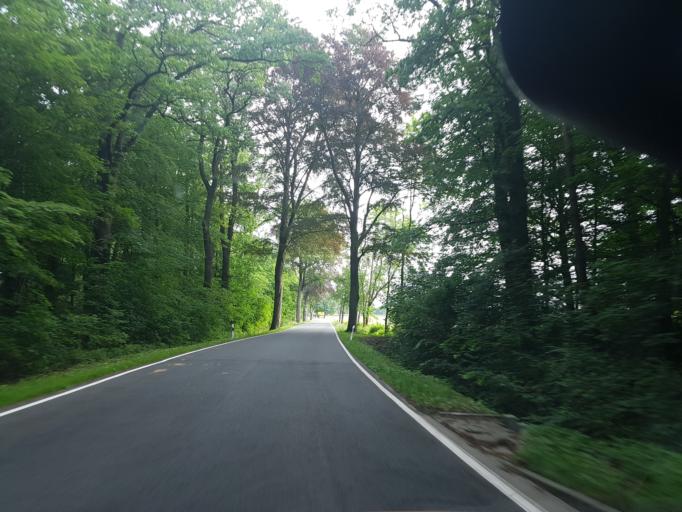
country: DE
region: Brandenburg
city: Sonnewalde
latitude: 51.6980
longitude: 13.6220
